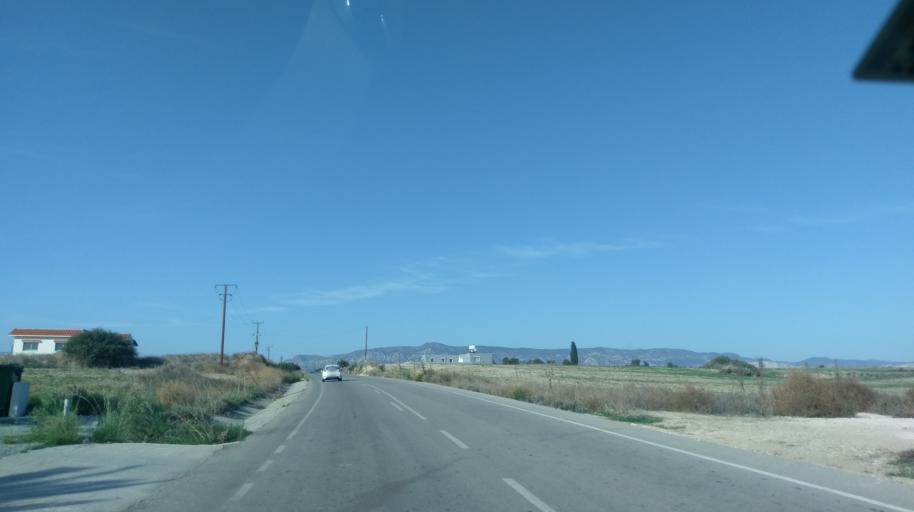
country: CY
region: Ammochostos
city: Lefkonoiko
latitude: 35.2633
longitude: 33.7474
